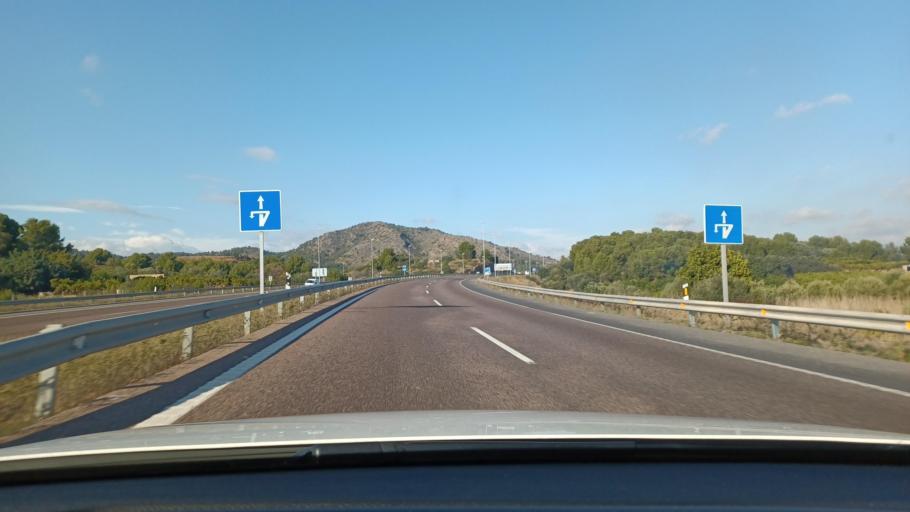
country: ES
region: Valencia
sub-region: Provincia de Castello
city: Villavieja
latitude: 39.8896
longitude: -0.1972
